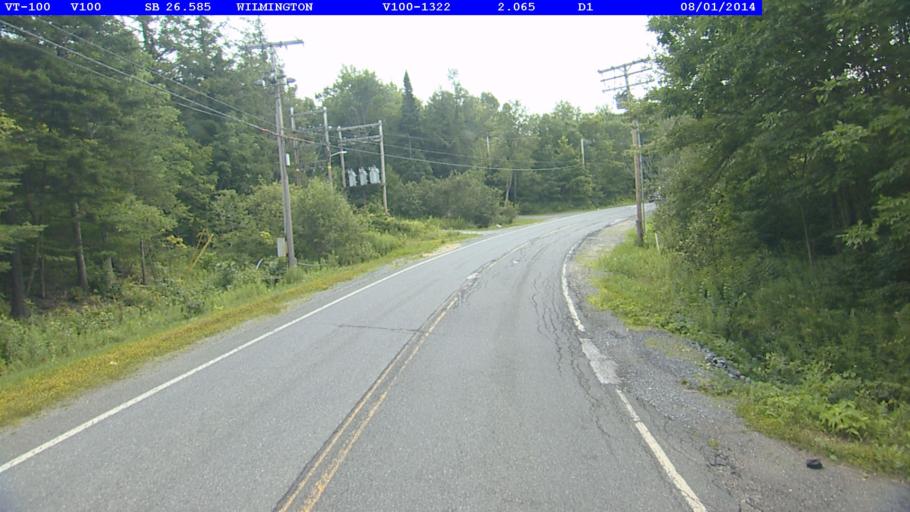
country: US
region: Vermont
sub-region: Windham County
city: Dover
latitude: 42.8550
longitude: -72.8543
